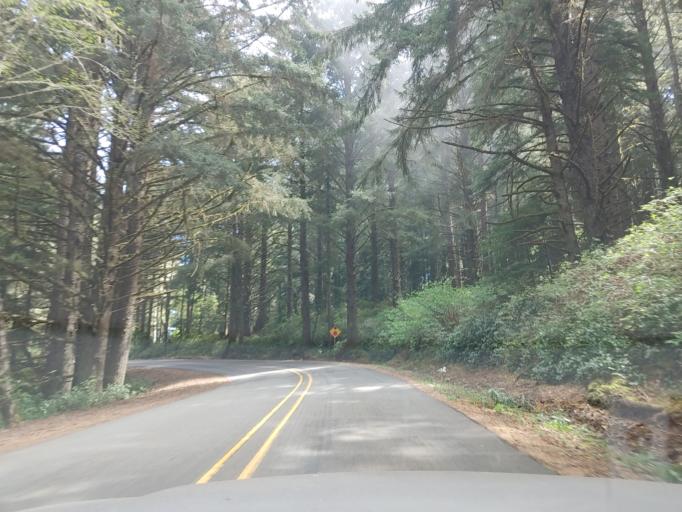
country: US
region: Oregon
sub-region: Coos County
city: Lakeside
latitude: 43.6644
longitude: -124.1906
